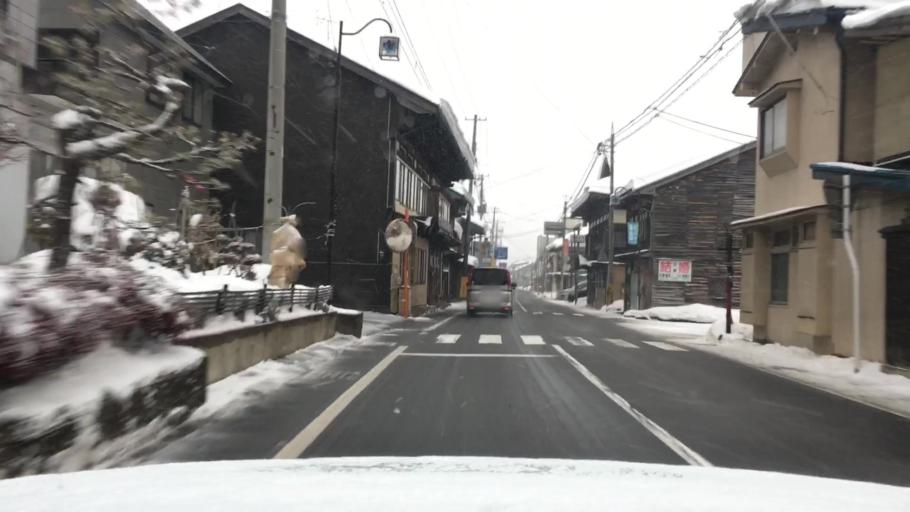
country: JP
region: Iwate
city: Ichinohe
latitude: 40.0978
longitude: 141.0476
